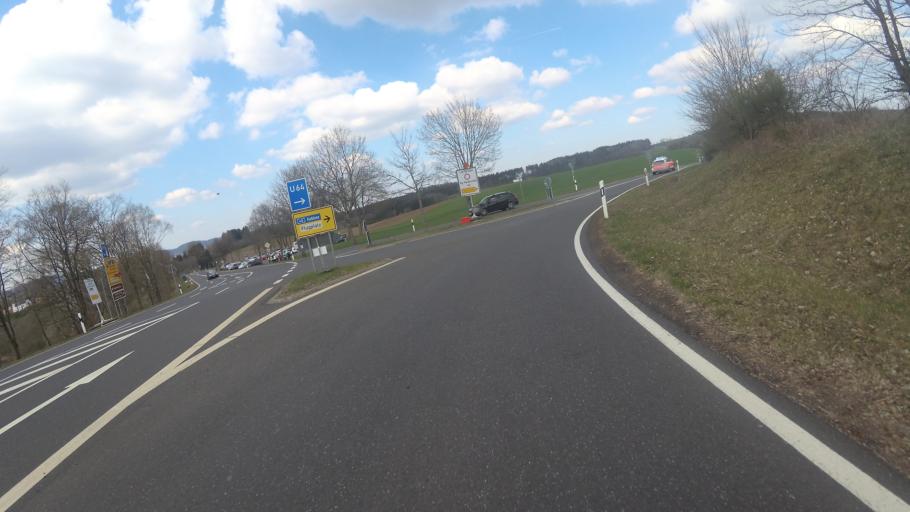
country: DE
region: Rheinland-Pfalz
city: Schalkenmehren
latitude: 50.1773
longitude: 6.8541
